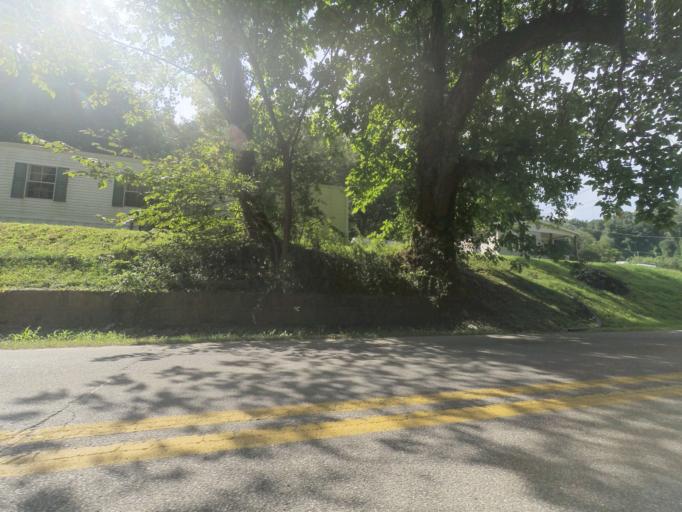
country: US
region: West Virginia
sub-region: Wayne County
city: Ceredo
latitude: 38.3842
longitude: -82.5616
